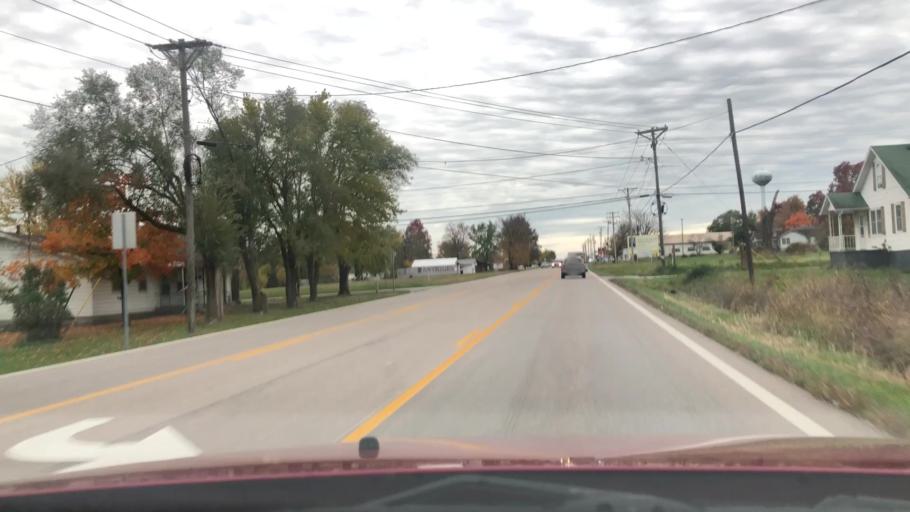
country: US
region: Missouri
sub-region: Dallas County
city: Buffalo
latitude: 37.6482
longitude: -93.1041
